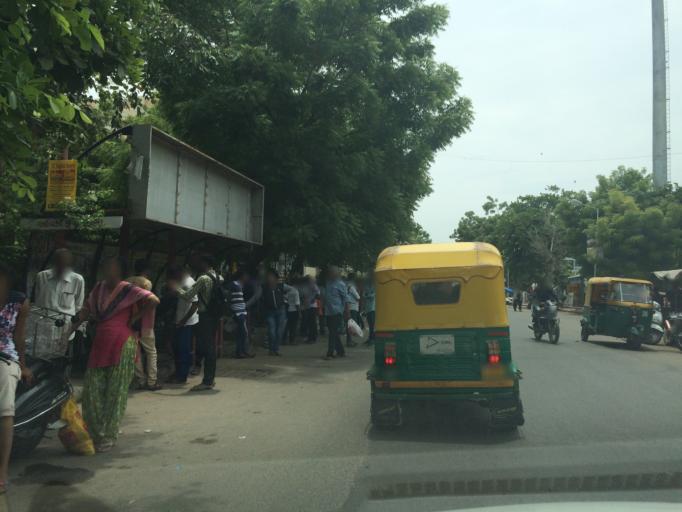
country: IN
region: Gujarat
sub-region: Ahmadabad
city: Ahmedabad
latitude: 23.0807
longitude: 72.5641
